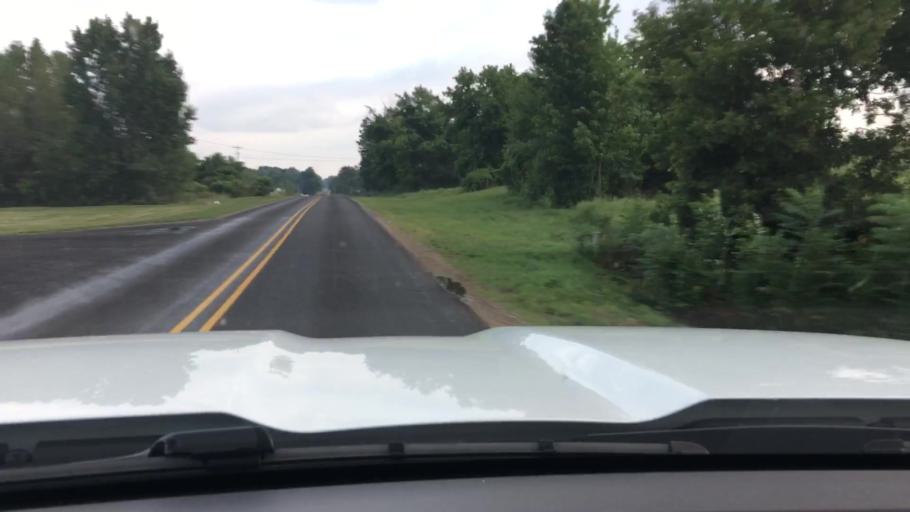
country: US
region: Michigan
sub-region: Ottawa County
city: Hudsonville
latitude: 42.8041
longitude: -85.8814
